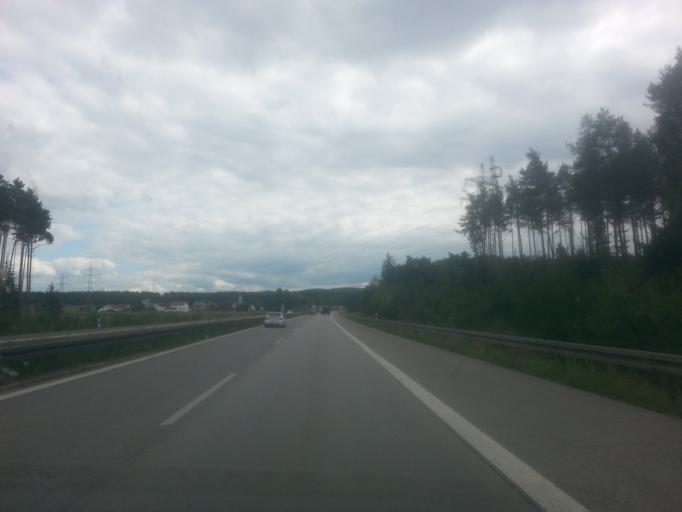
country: DE
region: Bavaria
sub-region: Upper Palatinate
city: Teublitz
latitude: 49.2506
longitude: 12.1275
